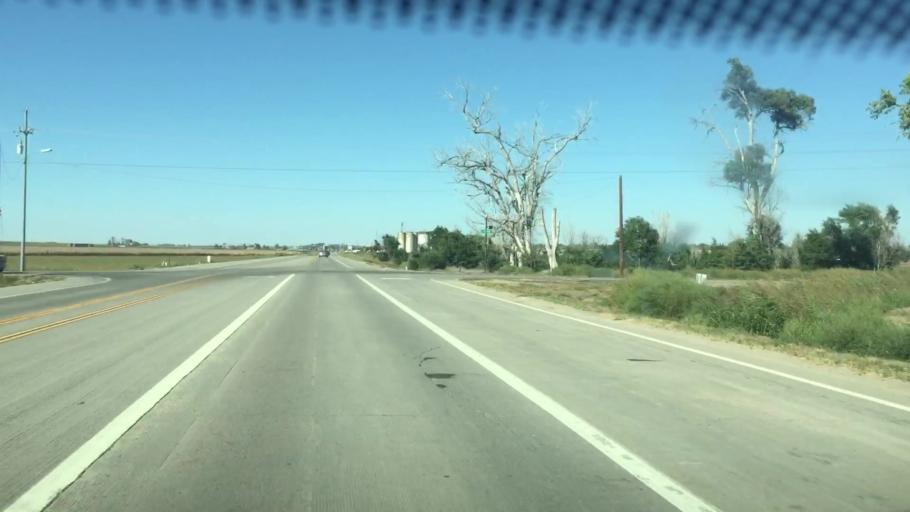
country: US
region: Colorado
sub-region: Prowers County
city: Lamar
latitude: 38.1427
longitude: -102.7237
